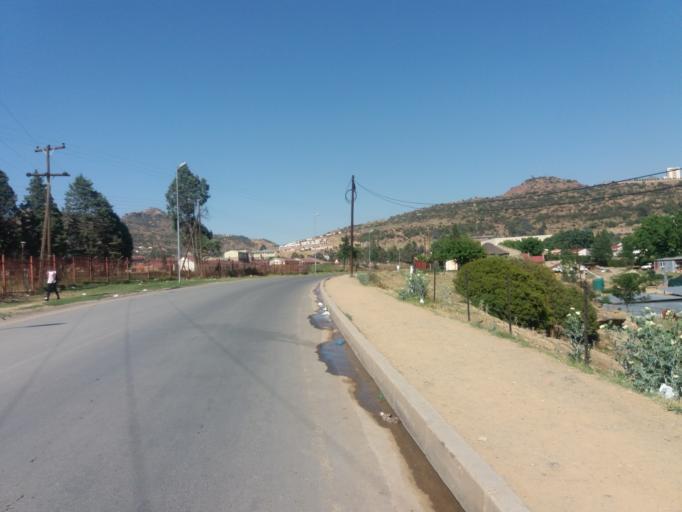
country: LS
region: Maseru
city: Maseru
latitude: -29.3218
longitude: 27.5034
